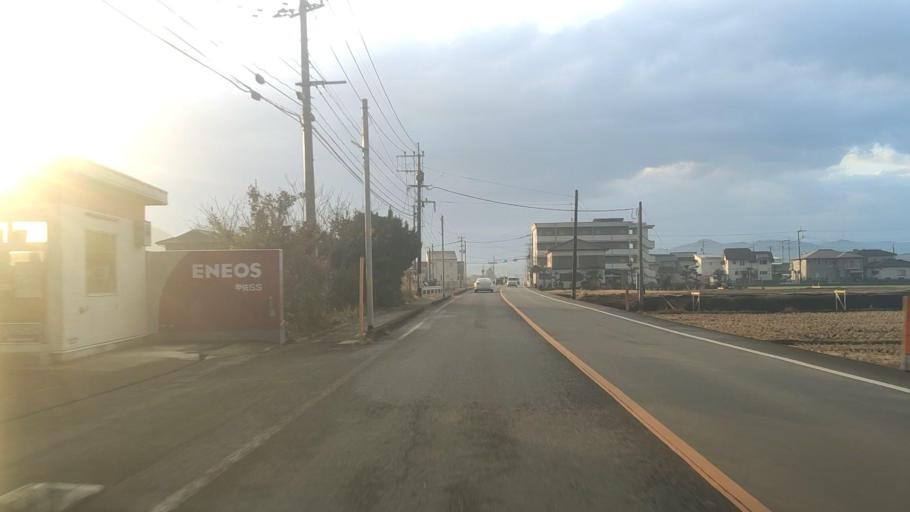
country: JP
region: Kumamoto
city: Uto
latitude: 32.7140
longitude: 130.7737
